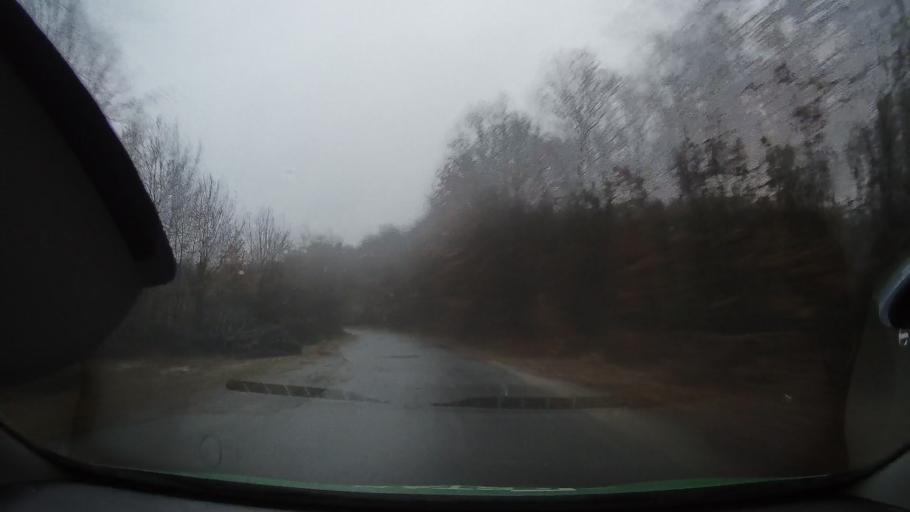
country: RO
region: Hunedoara
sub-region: Comuna Ribita
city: Ribita
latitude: 46.2349
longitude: 22.7504
